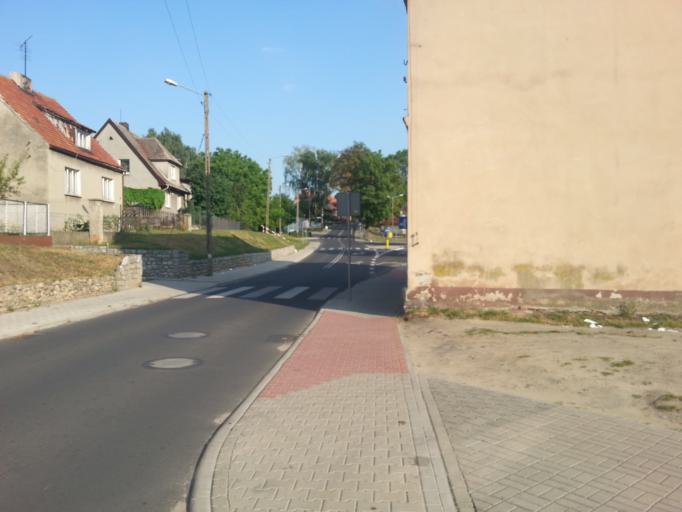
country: PL
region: Lower Silesian Voivodeship
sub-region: Powiat olesnicki
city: Twardogora
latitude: 51.3674
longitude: 17.4690
